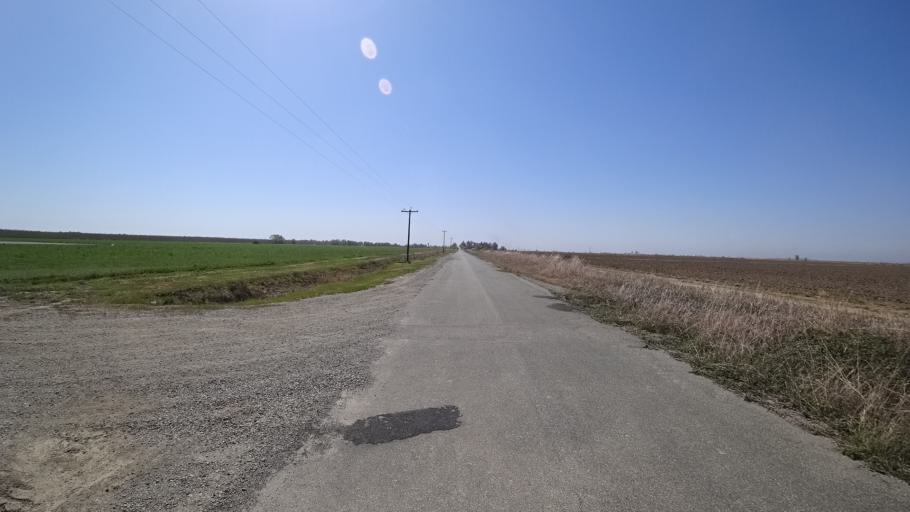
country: US
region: California
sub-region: Glenn County
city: Willows
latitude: 39.5037
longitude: -122.0373
